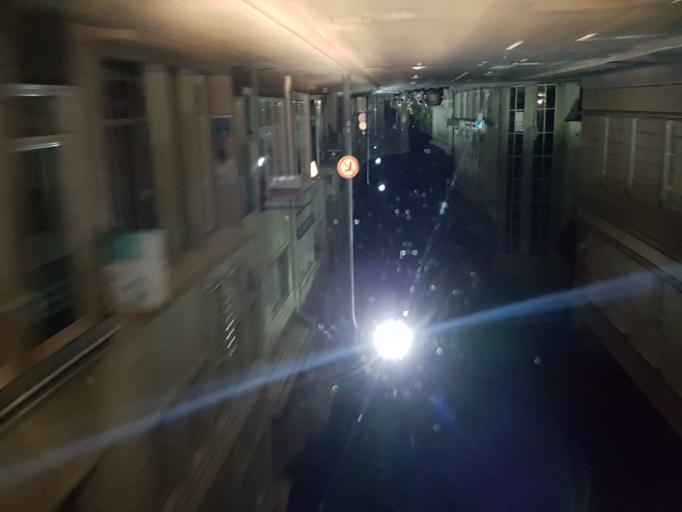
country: HU
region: Zala
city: Zalaegerszeg
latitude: 46.8433
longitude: 16.8441
